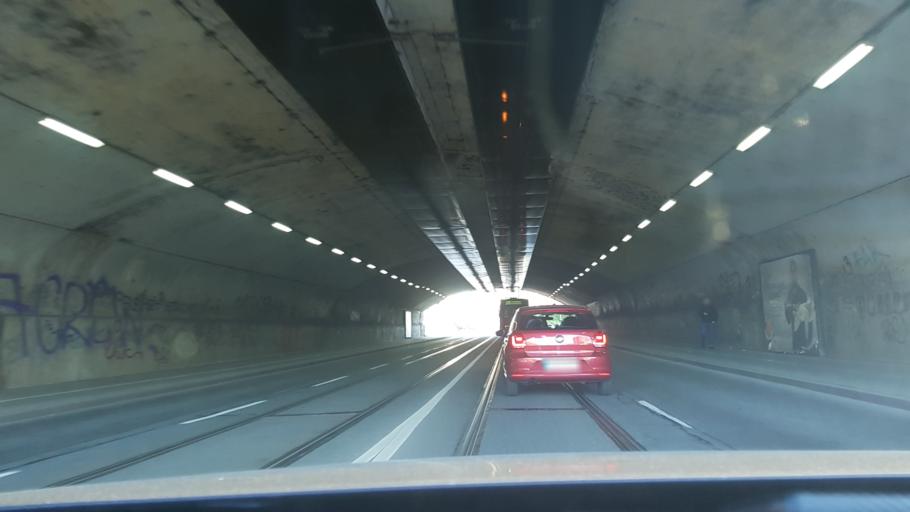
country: DE
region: North Rhine-Westphalia
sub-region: Regierungsbezirk Dusseldorf
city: Hochfeld
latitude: 51.4151
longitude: 6.7699
